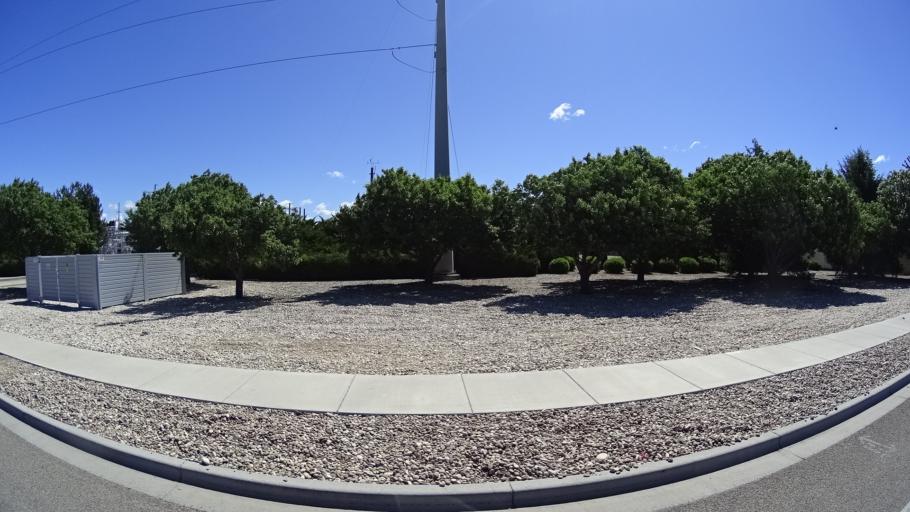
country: US
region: Idaho
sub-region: Ada County
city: Meridian
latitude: 43.6473
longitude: -116.3745
